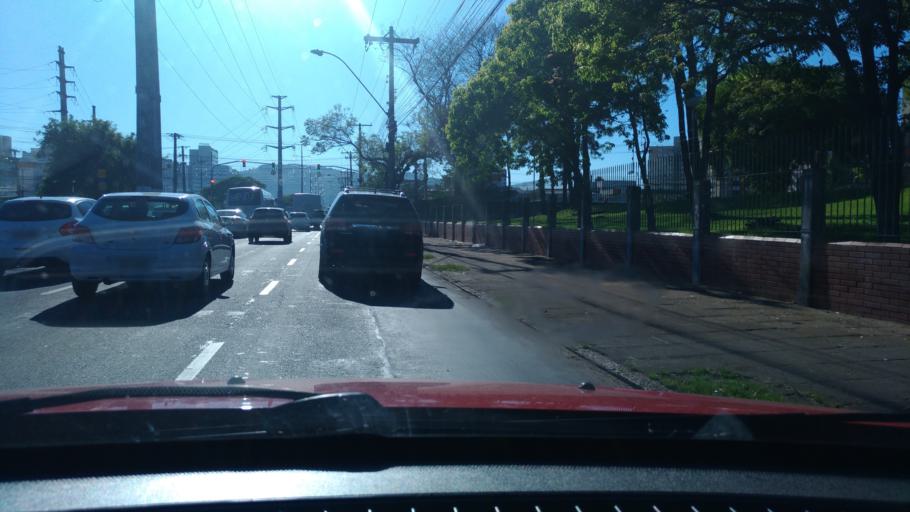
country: BR
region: Rio Grande do Sul
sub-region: Porto Alegre
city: Porto Alegre
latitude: -30.0560
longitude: -51.1701
